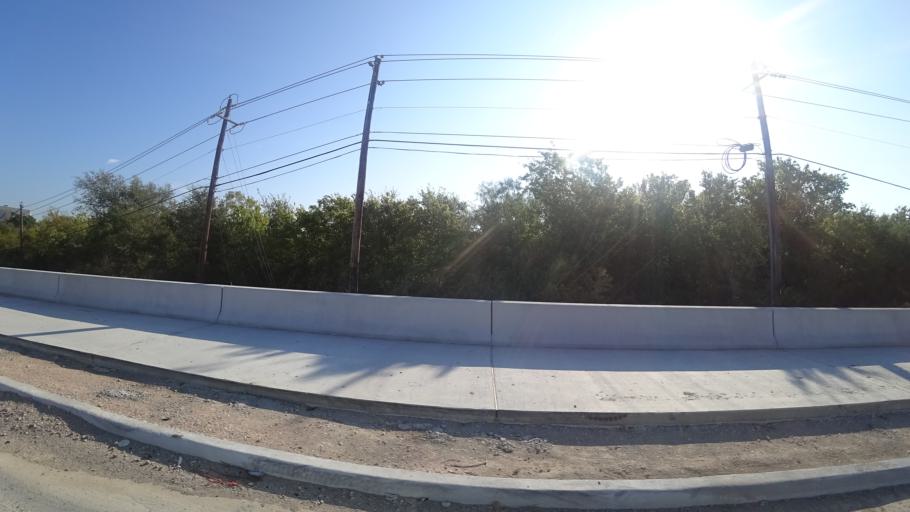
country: US
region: Texas
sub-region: Travis County
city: Austin
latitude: 30.3143
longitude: -97.6621
